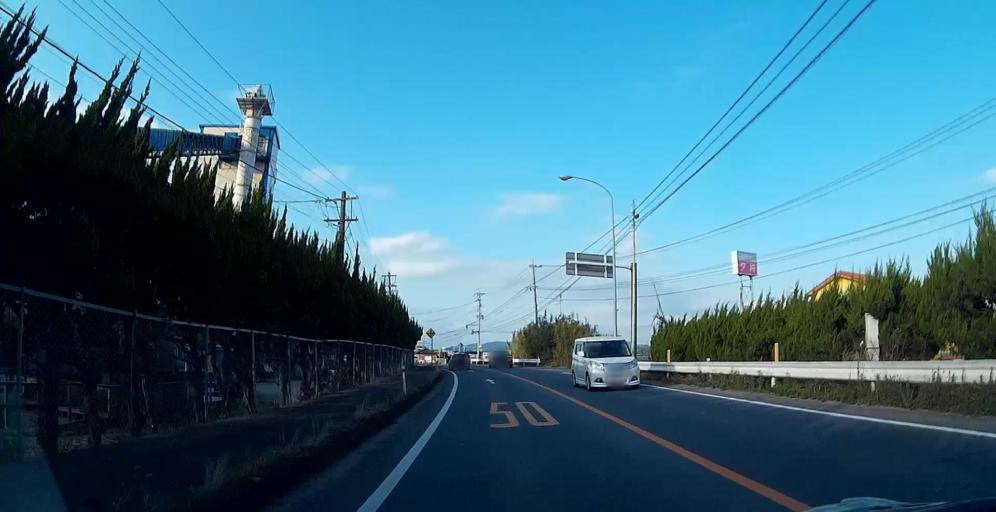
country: JP
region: Kumamoto
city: Matsubase
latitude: 32.6101
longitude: 130.7056
